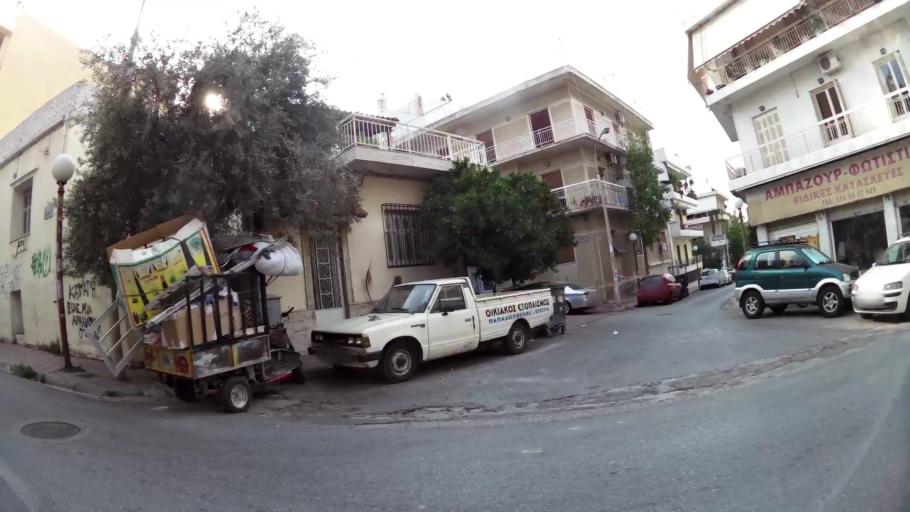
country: GR
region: Attica
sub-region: Nomarchia Athinas
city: Dhafni
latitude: 37.9500
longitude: 23.7266
